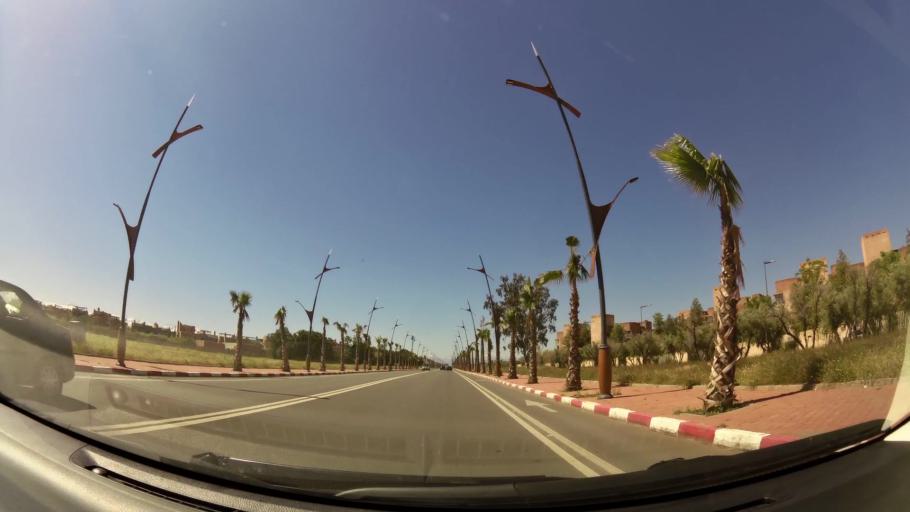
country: MA
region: Marrakech-Tensift-Al Haouz
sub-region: Marrakech
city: Marrakesh
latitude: 31.6017
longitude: -8.0007
